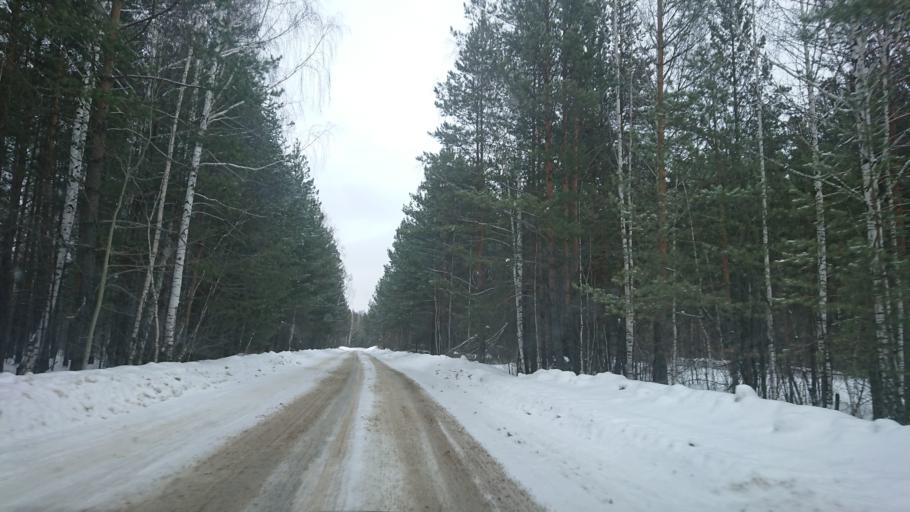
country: RU
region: Sverdlovsk
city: Sysert'
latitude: 56.4446
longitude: 60.8839
